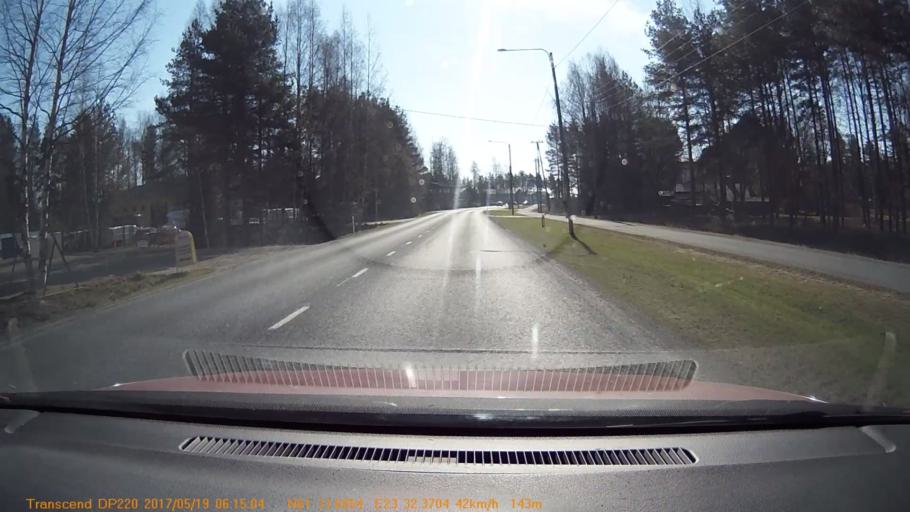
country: FI
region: Pirkanmaa
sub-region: Tampere
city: Yloejaervi
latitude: 61.5615
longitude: 23.5391
